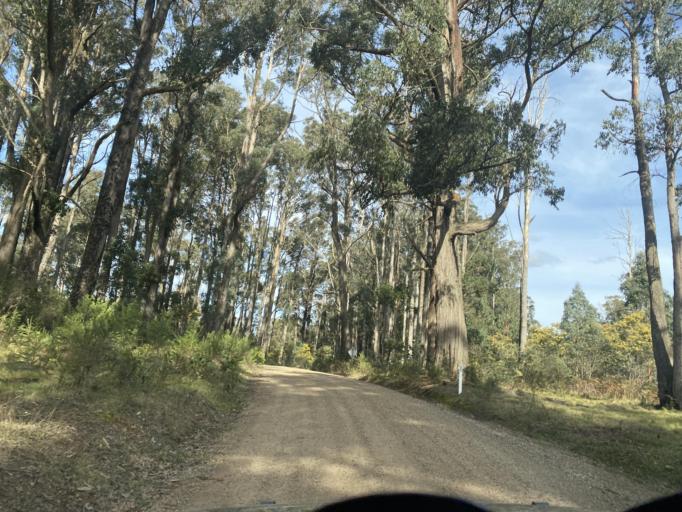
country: AU
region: Victoria
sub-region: Mansfield
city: Mansfield
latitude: -36.8486
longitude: 146.1814
